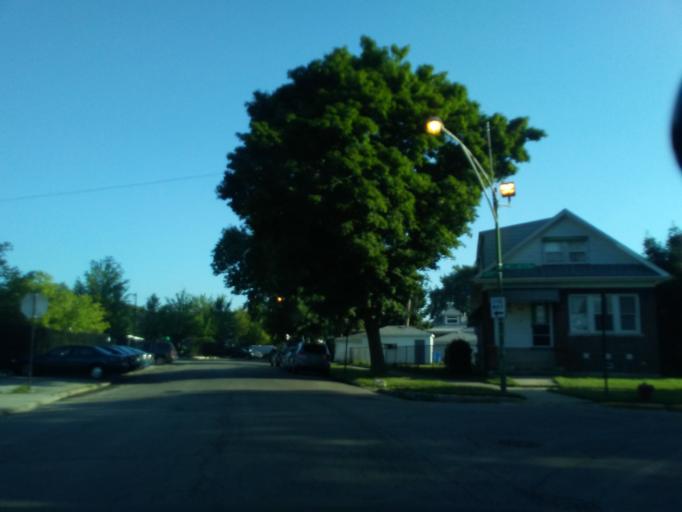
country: US
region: Illinois
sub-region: Cook County
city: Lincolnwood
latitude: 41.9353
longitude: -87.7326
